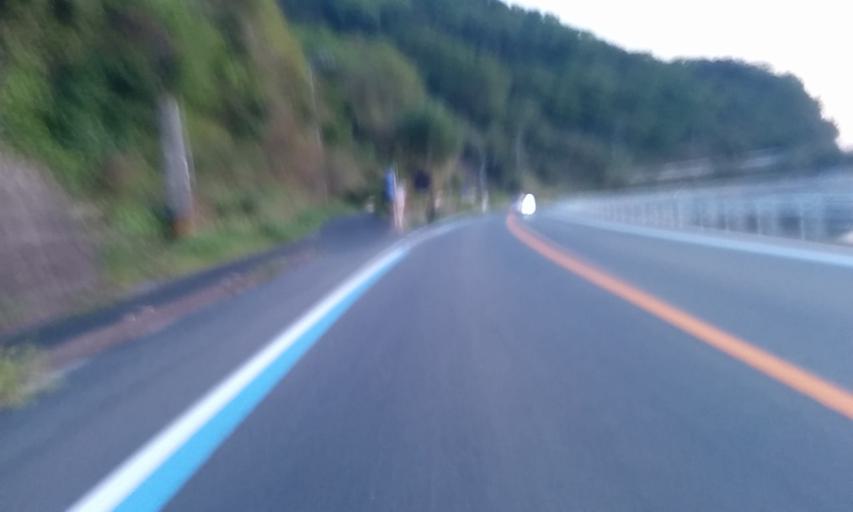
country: JP
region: Ehime
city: Ozu
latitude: 33.6047
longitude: 132.4726
